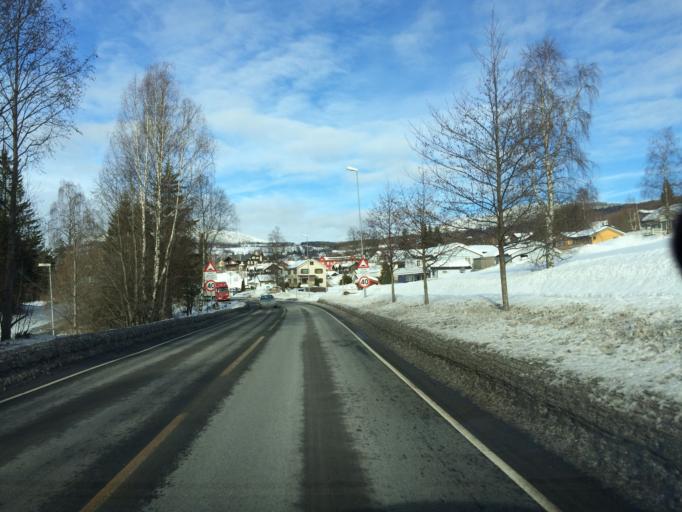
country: NO
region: Oppland
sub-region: Gausdal
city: Segalstad bru
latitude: 61.2127
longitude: 10.2929
